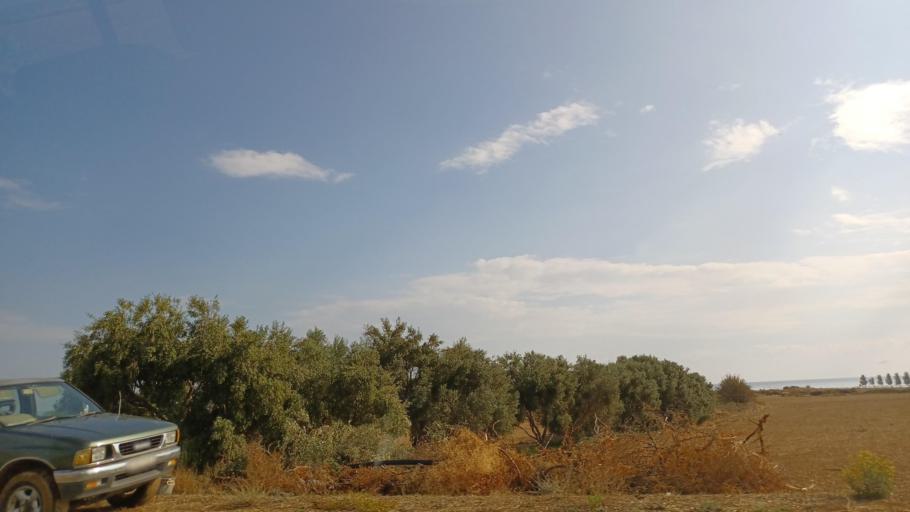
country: CY
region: Larnaka
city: Tersefanou
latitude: 34.8173
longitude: 33.5376
